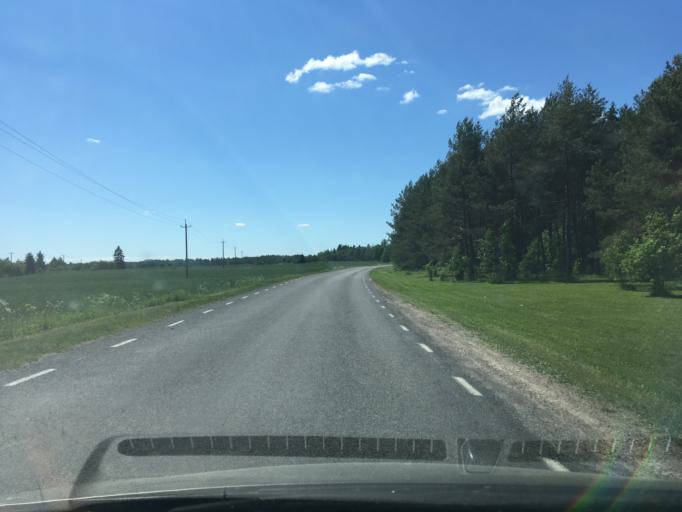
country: EE
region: Raplamaa
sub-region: Kohila vald
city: Kohila
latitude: 59.1420
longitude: 24.8486
